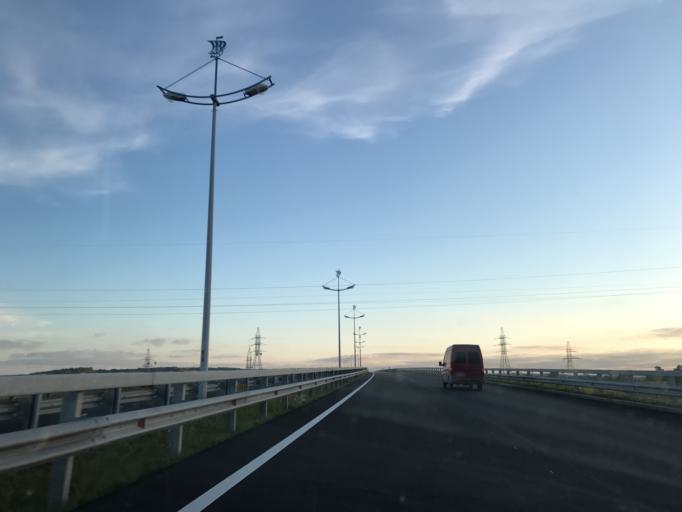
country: RU
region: Kaliningrad
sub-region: Gorod Kaliningrad
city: Pionerskiy
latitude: 54.9169
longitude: 20.2380
